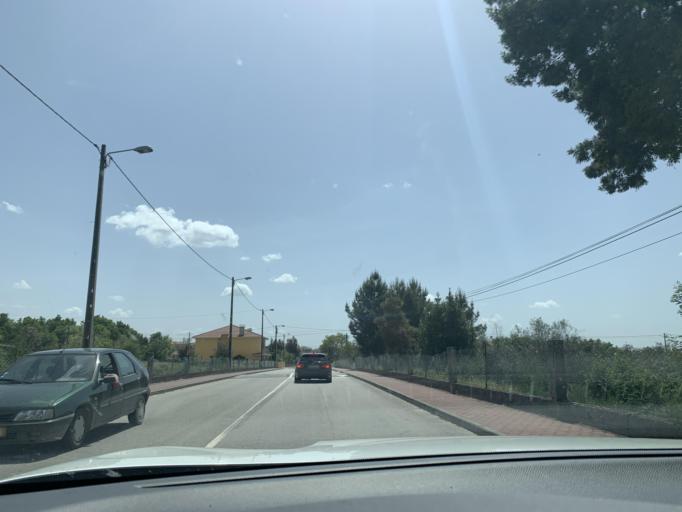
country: PT
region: Viseu
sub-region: Mangualde
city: Mangualde
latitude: 40.6087
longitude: -7.7470
